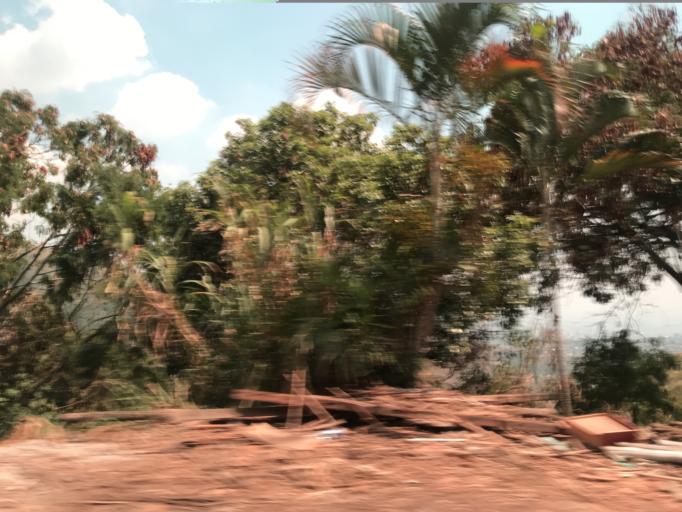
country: CO
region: Valle del Cauca
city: Cali
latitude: 3.4587
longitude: -76.5833
